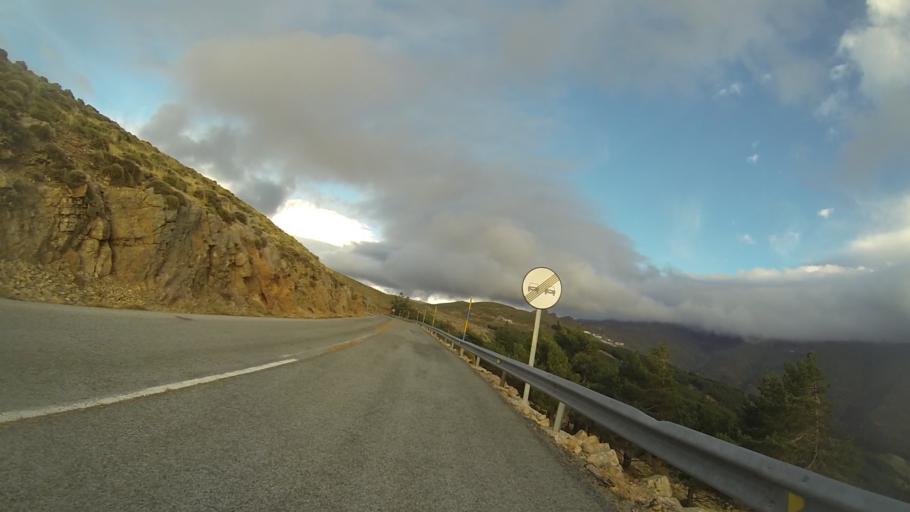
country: ES
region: Andalusia
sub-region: Provincia de Granada
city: Guejar-Sierra
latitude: 37.1169
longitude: -3.4297
